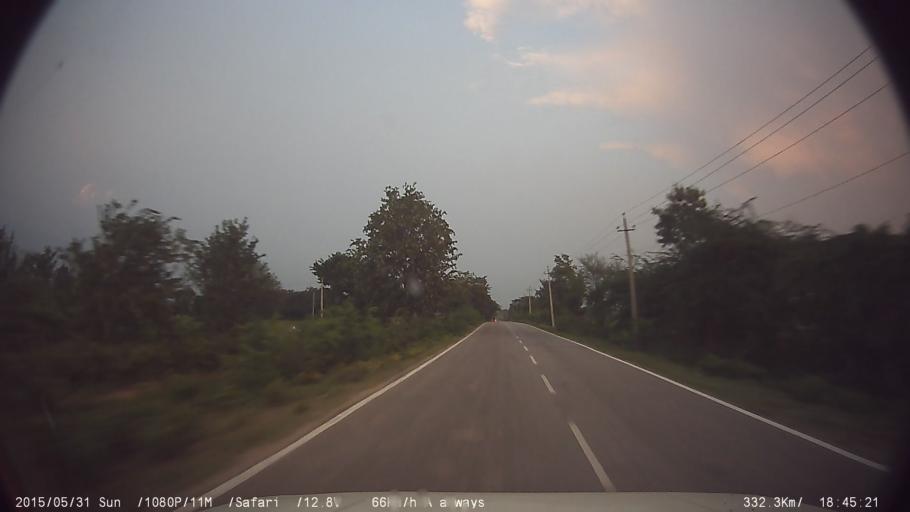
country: IN
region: Karnataka
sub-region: Mysore
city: Tirumakudal Narsipur
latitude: 12.1588
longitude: 76.8237
